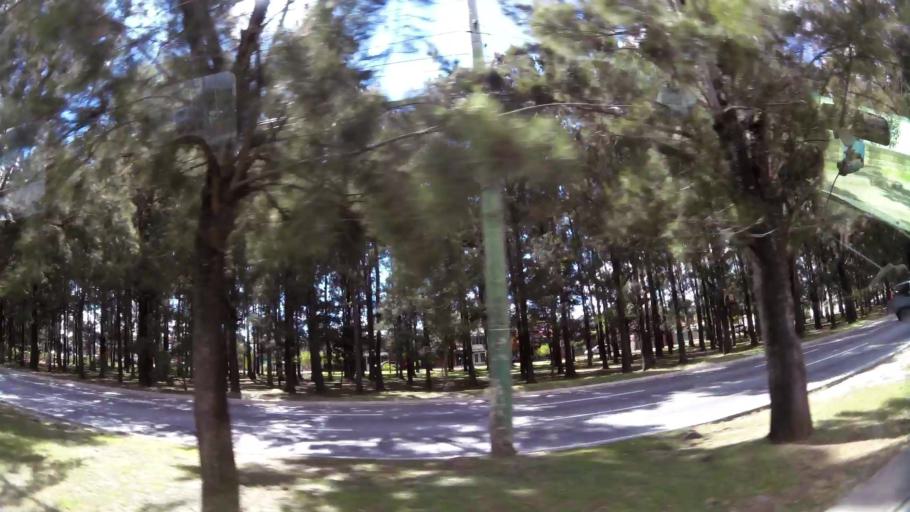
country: GT
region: Guatemala
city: Santa Catarina Pinula
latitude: 14.6025
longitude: -90.4999
